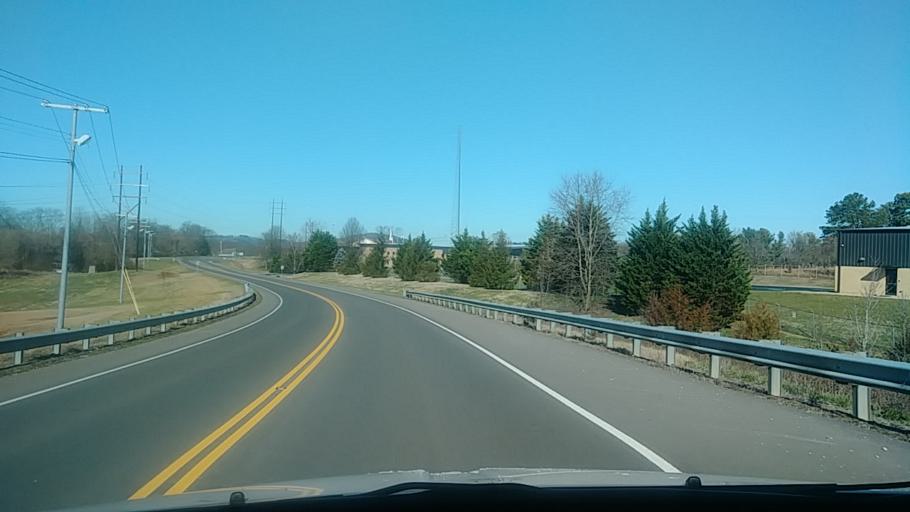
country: US
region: Tennessee
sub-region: Hamblen County
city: Morristown
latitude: 36.1932
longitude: -83.3061
